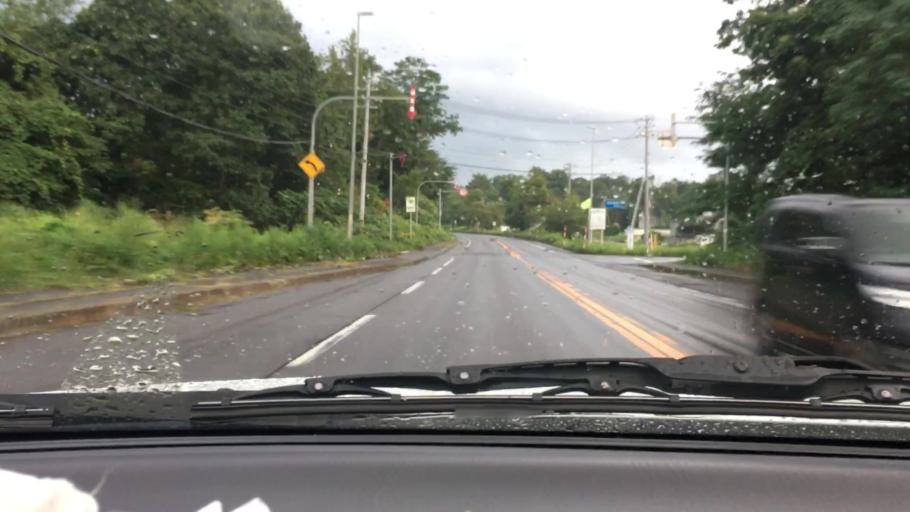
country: JP
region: Hokkaido
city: Nanae
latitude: 42.0842
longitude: 140.5855
